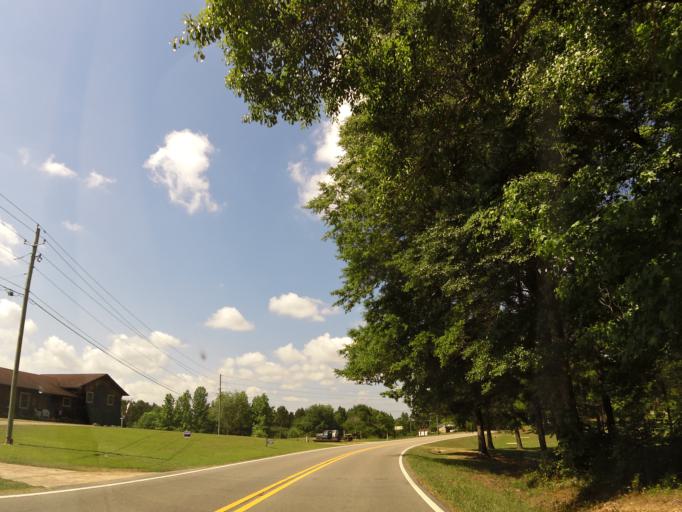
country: US
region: Alabama
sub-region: Marion County
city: Guin
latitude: 34.0073
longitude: -87.8541
